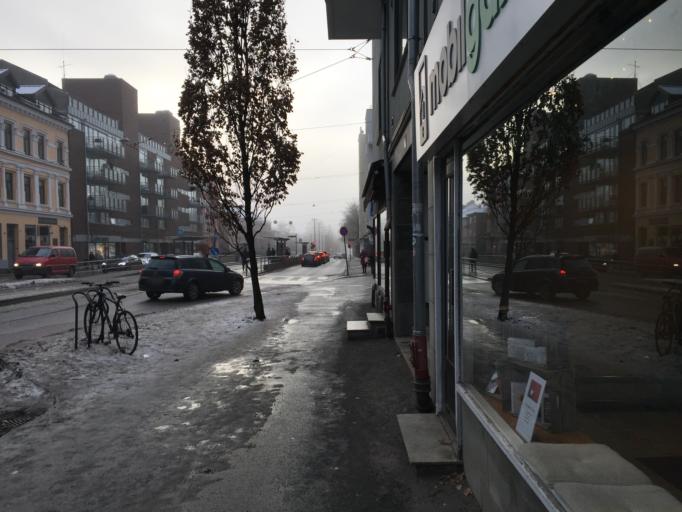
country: NO
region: Oslo
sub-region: Oslo
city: Sjolyststranda
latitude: 59.9279
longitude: 10.7134
